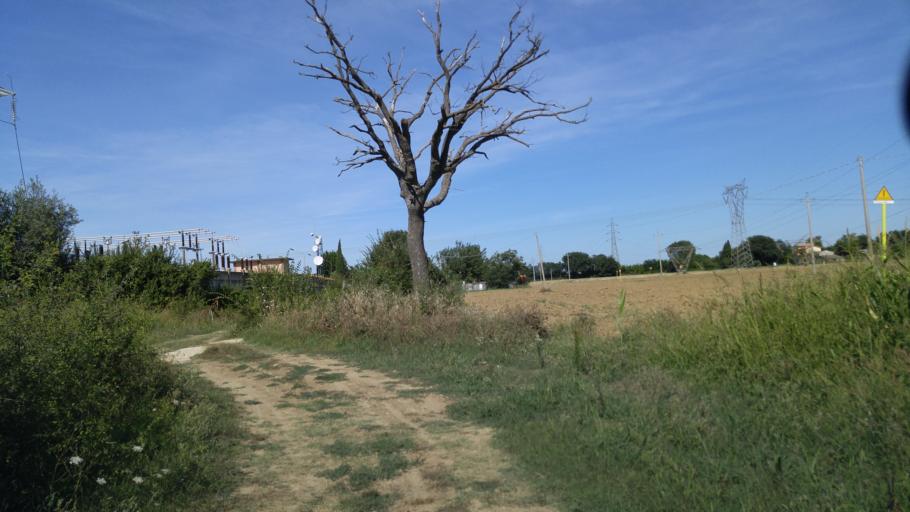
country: IT
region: The Marches
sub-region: Provincia di Pesaro e Urbino
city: Cuccurano
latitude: 43.7855
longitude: 12.9557
